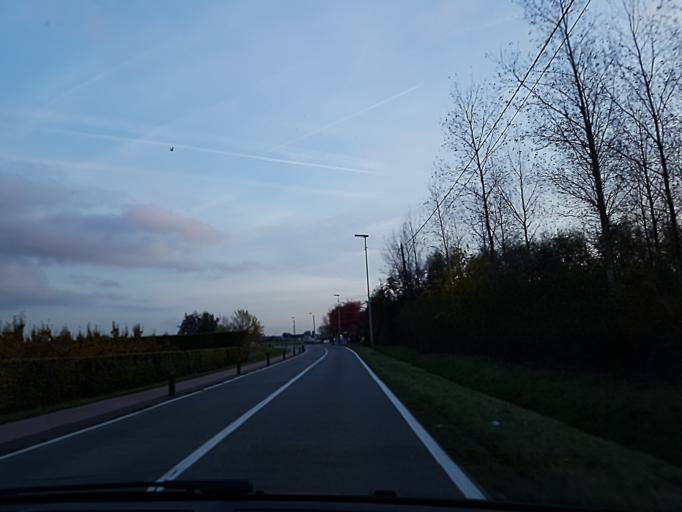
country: BE
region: Flanders
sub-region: Provincie Antwerpen
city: Ranst
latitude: 51.1685
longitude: 4.5646
